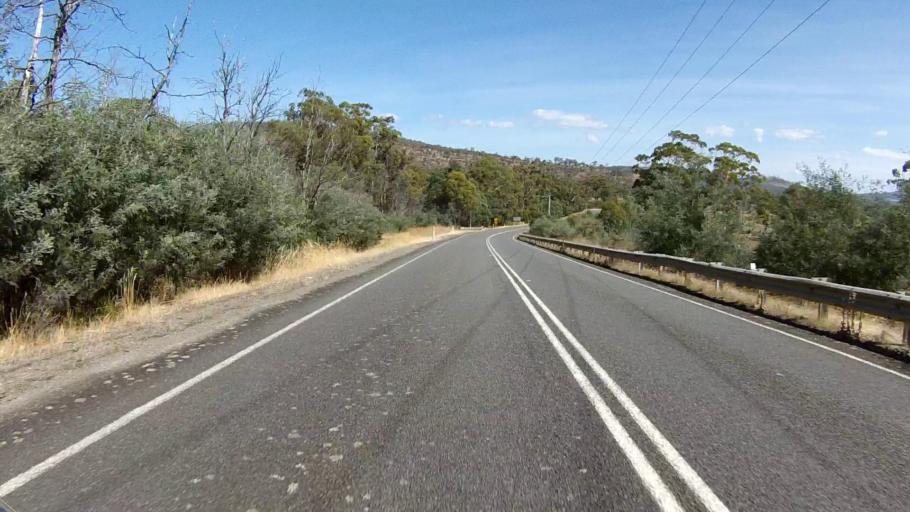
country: AU
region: Tasmania
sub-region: Sorell
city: Sorell
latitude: -42.5877
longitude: 147.8001
